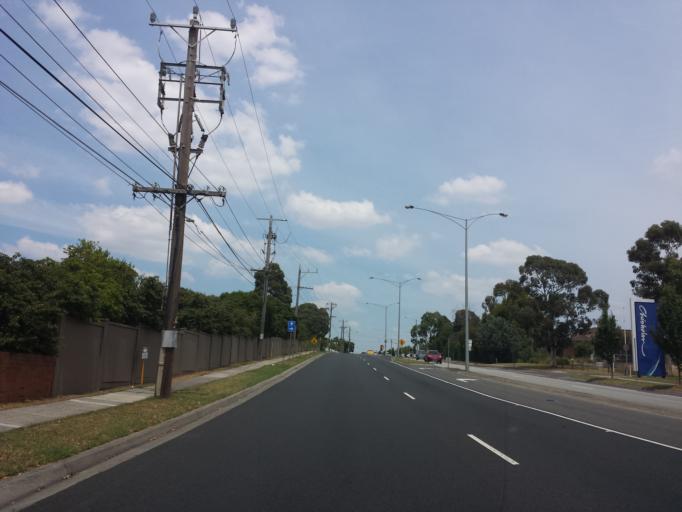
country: AU
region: Victoria
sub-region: Greater Dandenong
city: Dandenong North
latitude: -37.9756
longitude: 145.2227
